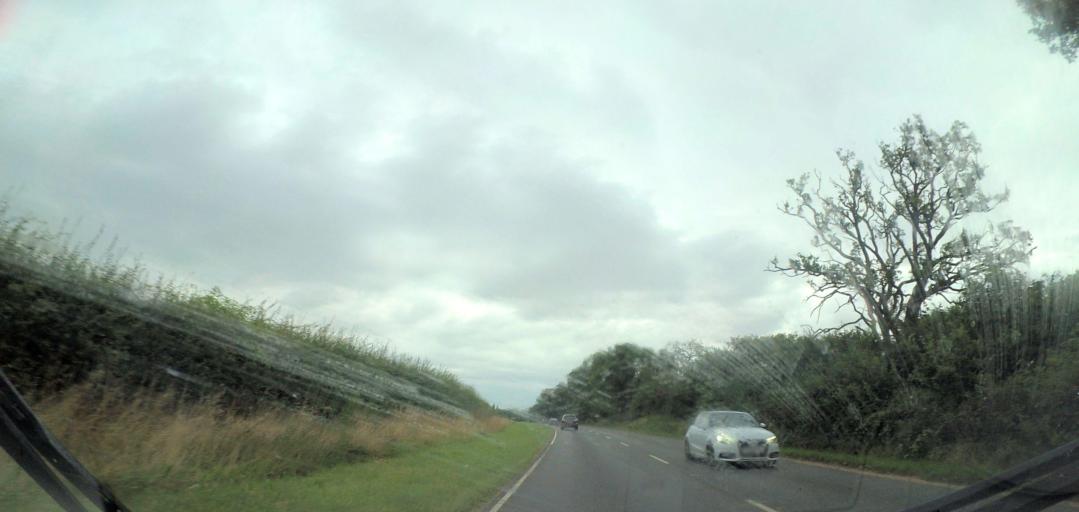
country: GB
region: England
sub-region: Norfolk
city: Coltishall
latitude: 52.7099
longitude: 1.3479
